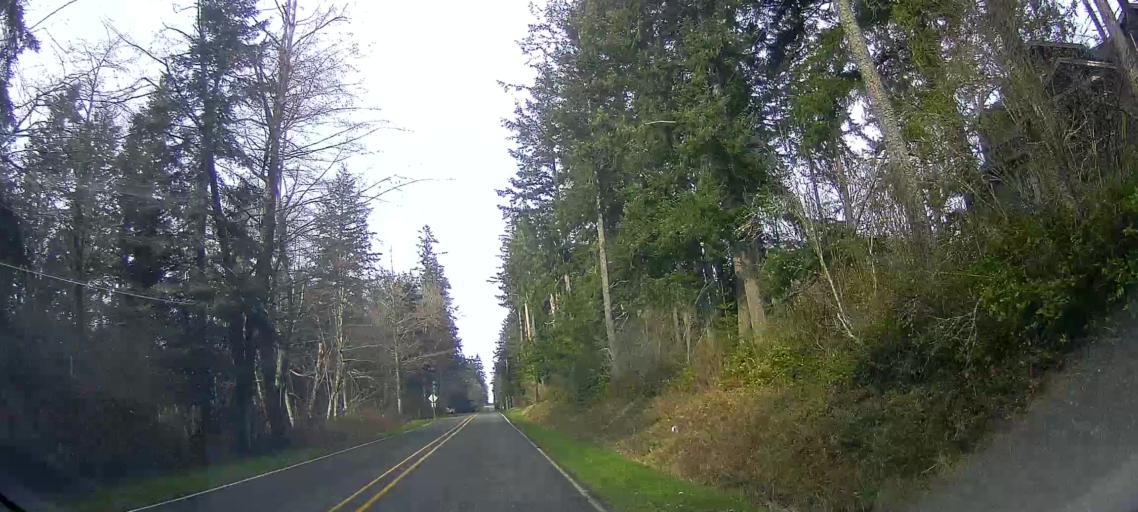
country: US
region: Washington
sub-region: Island County
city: Langley
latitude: 48.0624
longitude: -122.3652
